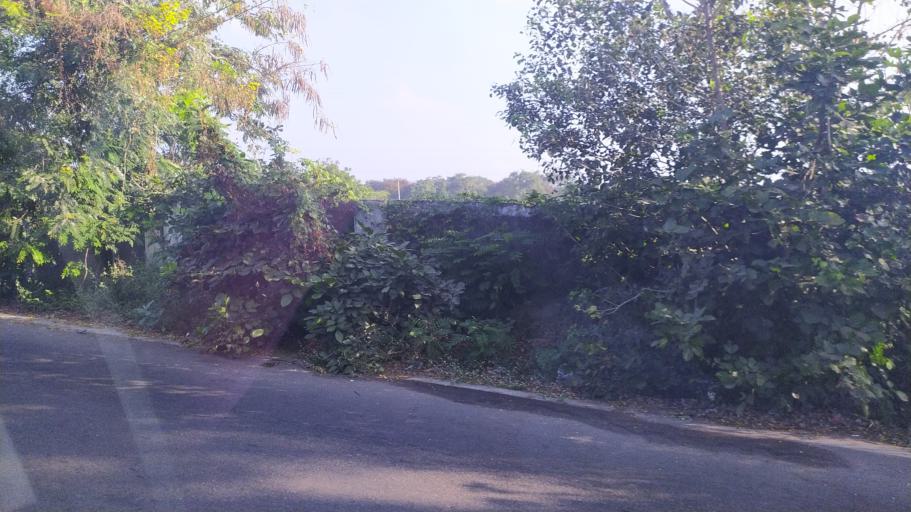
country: IN
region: Telangana
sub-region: Hyderabad
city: Hyderabad
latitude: 17.3276
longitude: 78.4187
